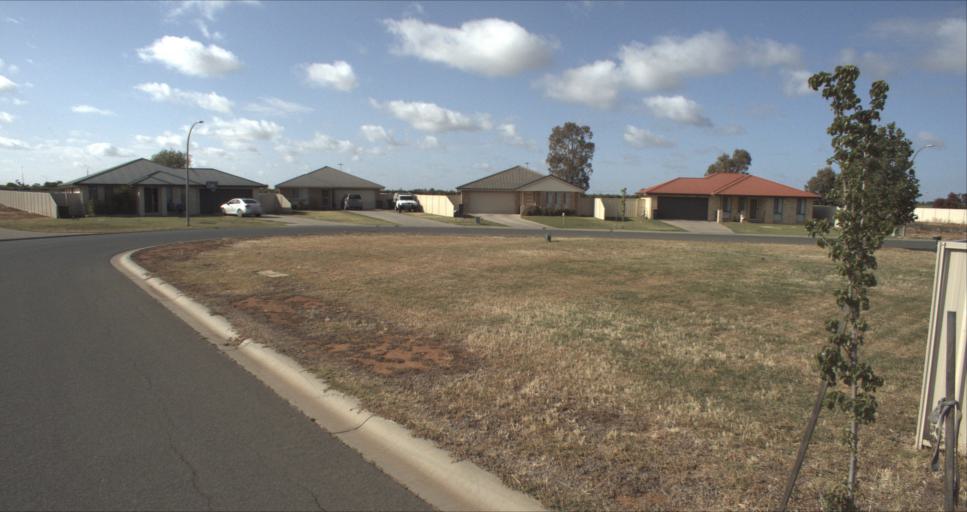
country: AU
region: New South Wales
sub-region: Leeton
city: Leeton
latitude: -34.5698
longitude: 146.4045
